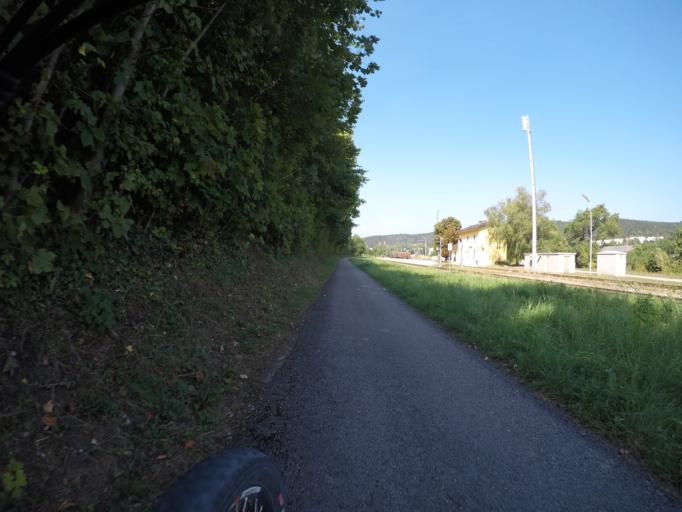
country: AT
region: Lower Austria
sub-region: Politischer Bezirk Baden
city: Berndorf
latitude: 47.9398
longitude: 16.1347
